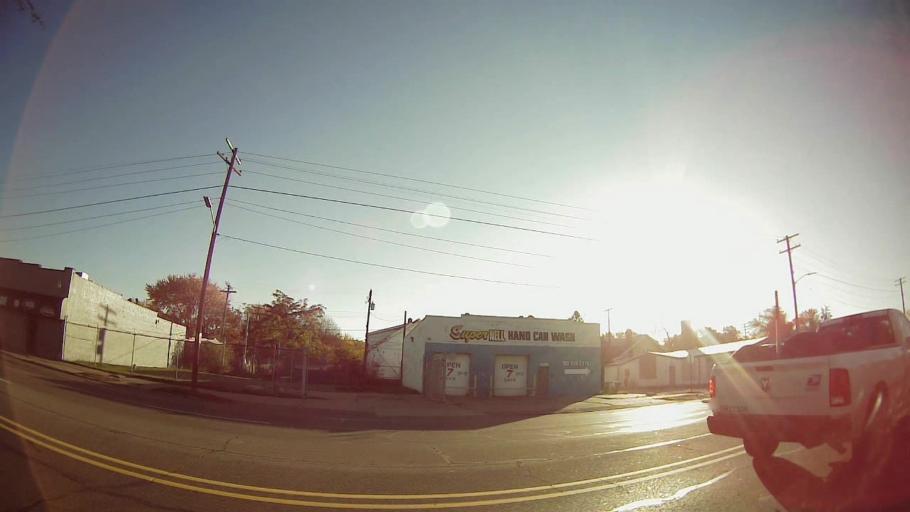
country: US
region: Michigan
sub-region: Wayne County
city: Hamtramck
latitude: 42.4286
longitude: -83.0242
